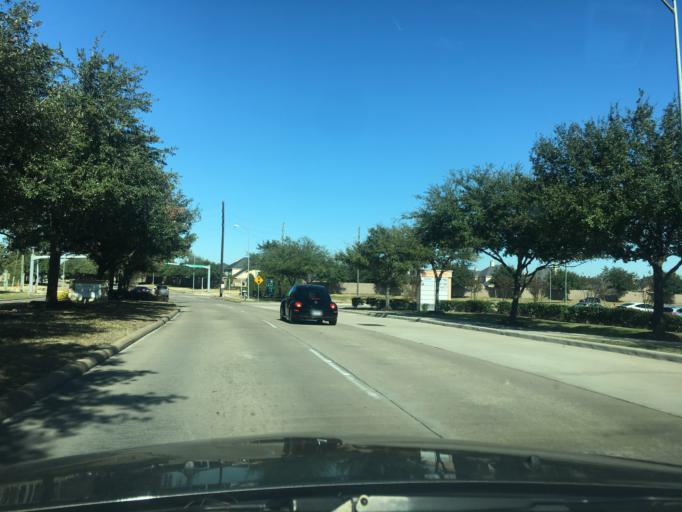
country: US
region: Texas
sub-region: Fort Bend County
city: Greatwood
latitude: 29.5590
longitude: -95.7156
